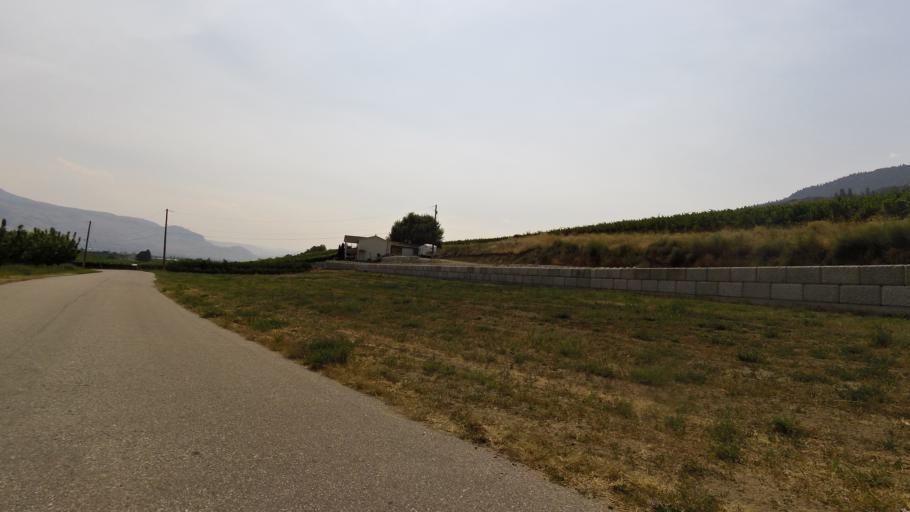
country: CA
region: British Columbia
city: Osoyoos
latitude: 49.0528
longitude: -119.5096
